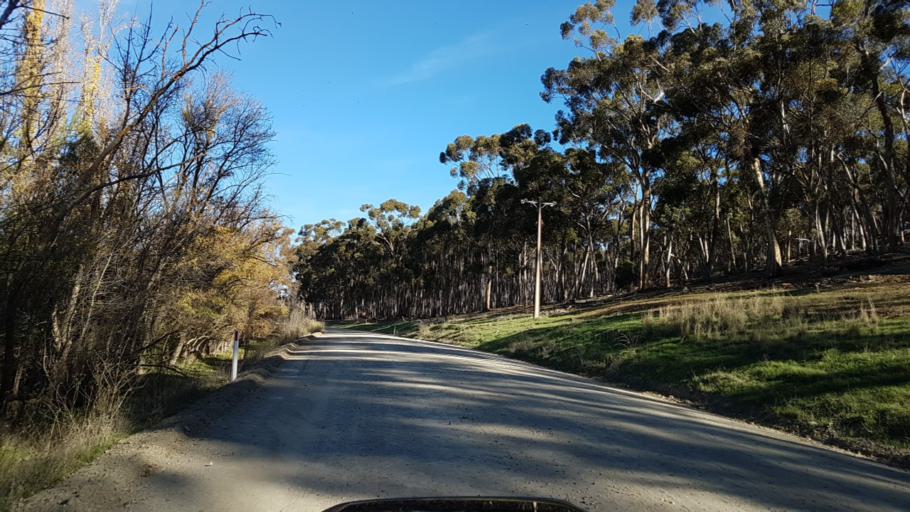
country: AU
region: South Australia
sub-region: Northern Areas
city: Jamestown
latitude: -33.2799
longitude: 138.5667
